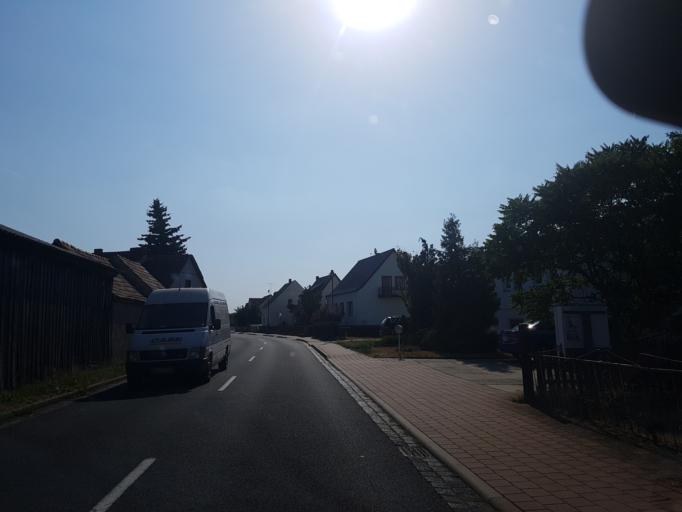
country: DE
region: Saxony-Anhalt
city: Annaburg
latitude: 51.7043
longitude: 13.0170
